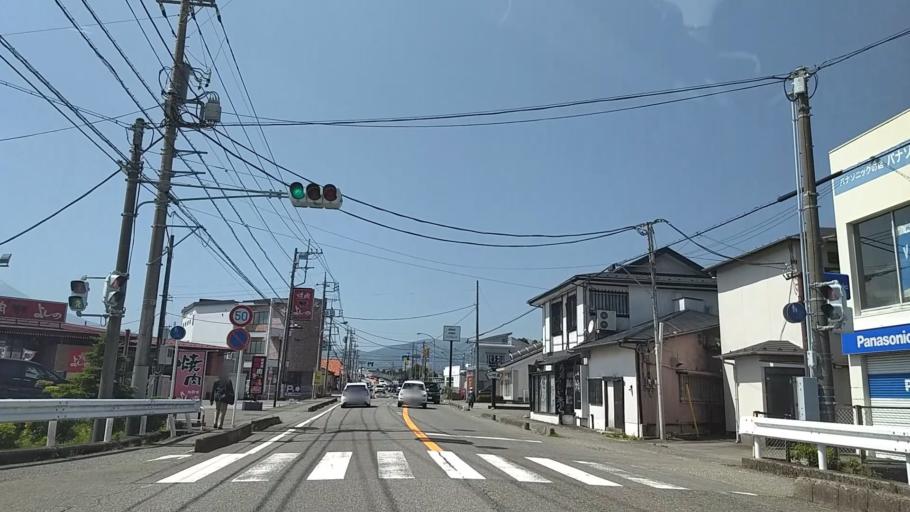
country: JP
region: Shizuoka
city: Gotemba
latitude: 35.2998
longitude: 138.9400
